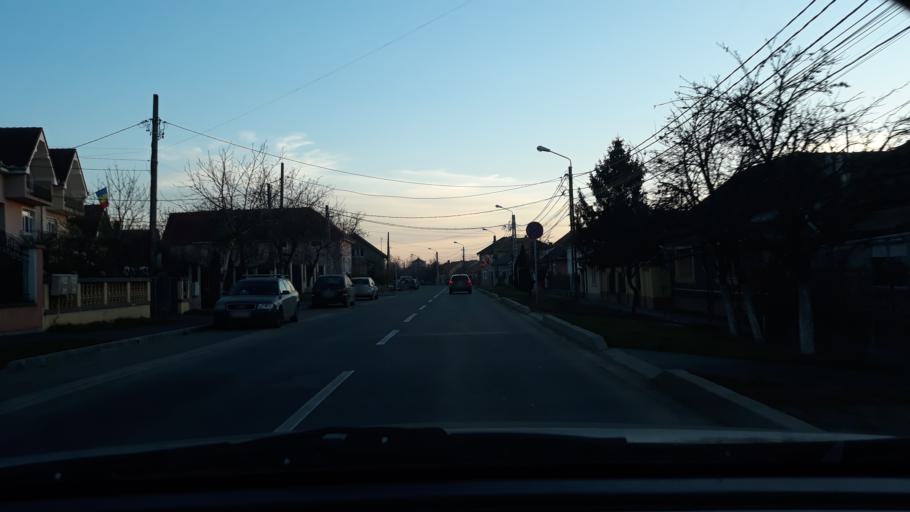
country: RO
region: Bihor
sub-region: Comuna Biharea
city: Oradea
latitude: 47.0876
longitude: 21.9267
